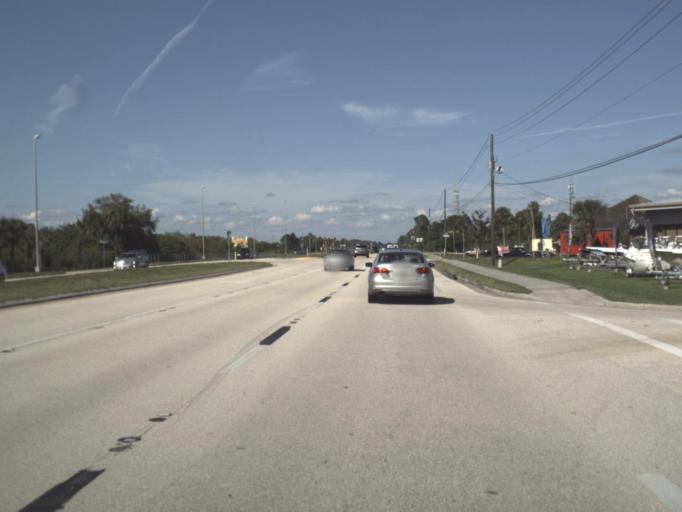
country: US
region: Florida
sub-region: Sarasota County
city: North Port
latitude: 26.9674
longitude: -82.2103
